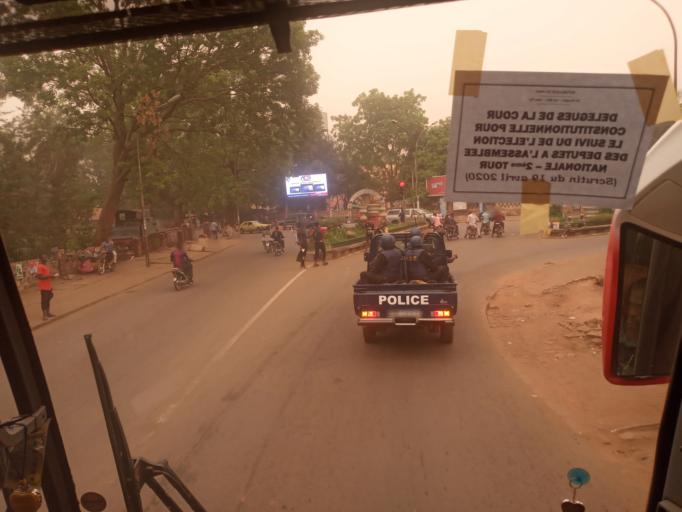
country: ML
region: Bamako
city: Bamako
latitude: 12.6497
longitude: -7.9987
